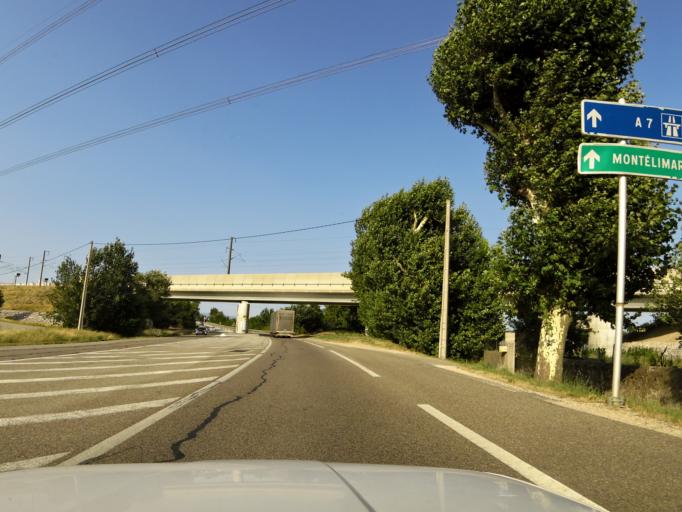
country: FR
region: Provence-Alpes-Cote d'Azur
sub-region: Departement du Vaucluse
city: Mondragon
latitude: 44.2690
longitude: 4.6951
